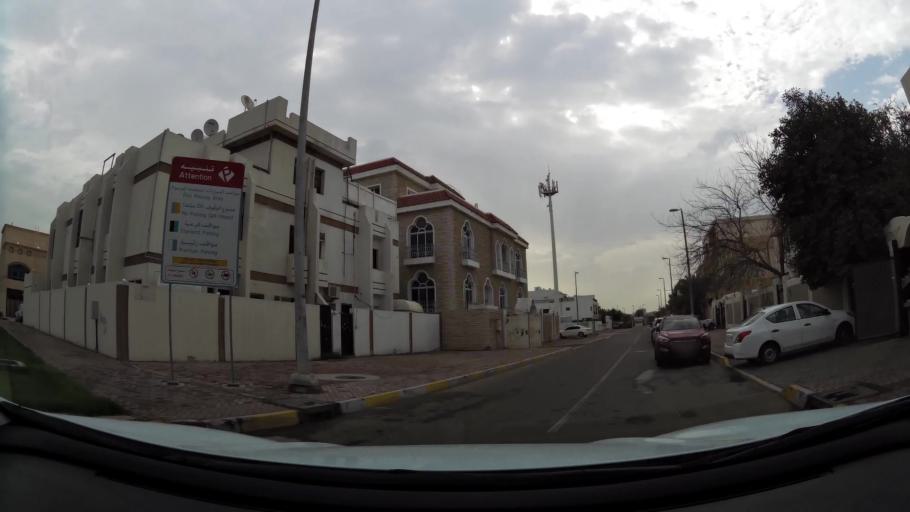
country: AE
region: Abu Dhabi
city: Abu Dhabi
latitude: 24.4531
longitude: 54.4009
